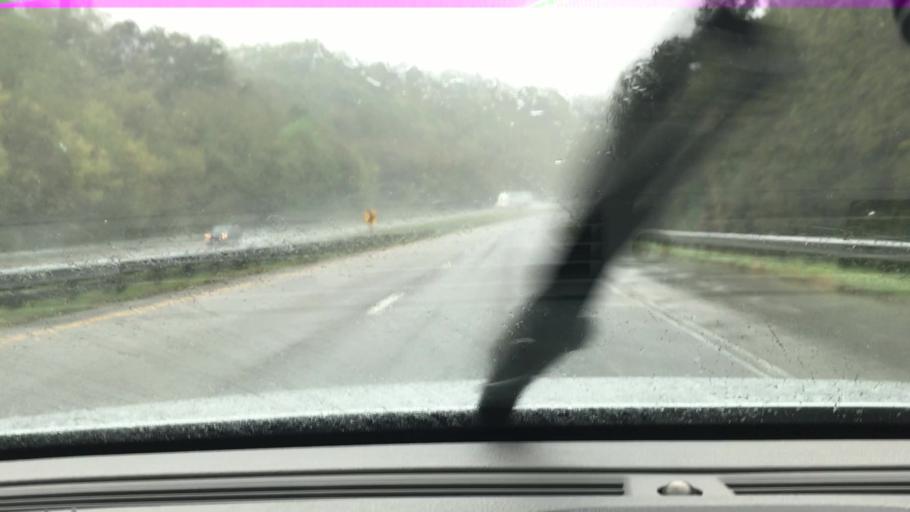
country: US
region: Alabama
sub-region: Limestone County
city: Ardmore
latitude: 34.9840
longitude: -86.8801
